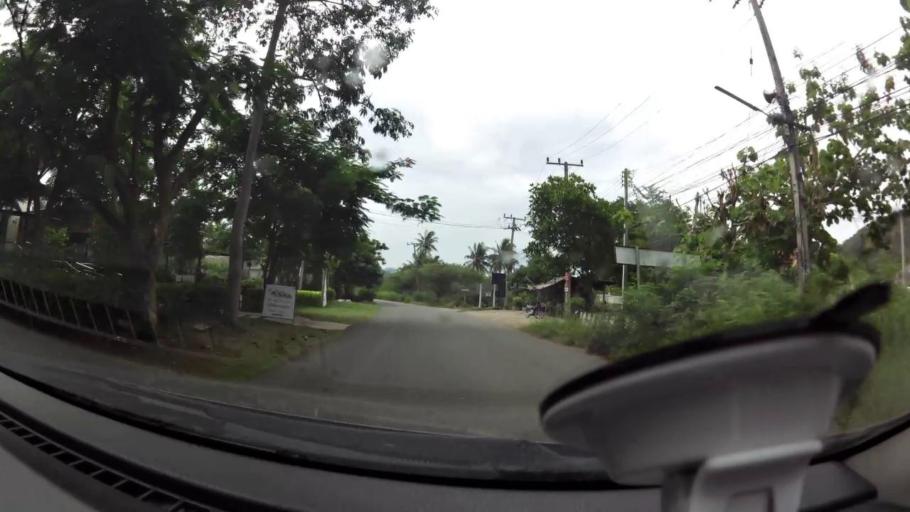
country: TH
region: Prachuap Khiri Khan
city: Pran Buri
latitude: 12.4436
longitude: 99.9695
